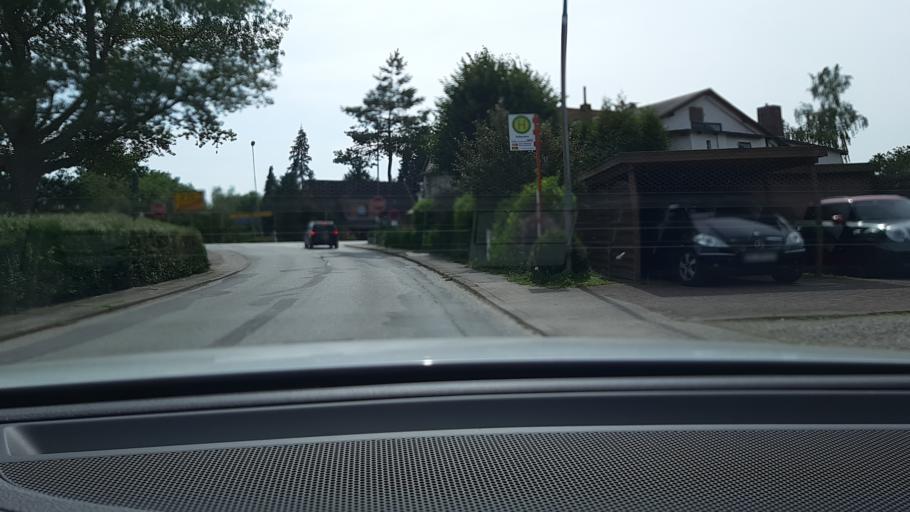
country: DE
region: Schleswig-Holstein
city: Reinfeld
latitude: 53.8223
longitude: 10.4732
